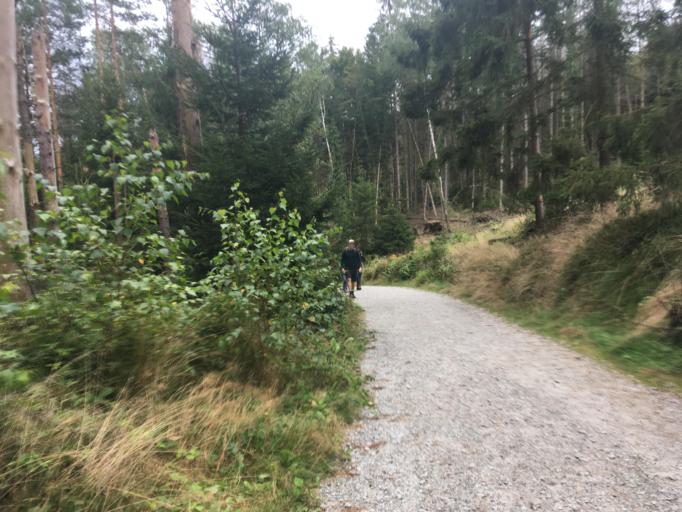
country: DE
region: Saxony
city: Sebnitz
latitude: 50.9204
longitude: 14.2376
